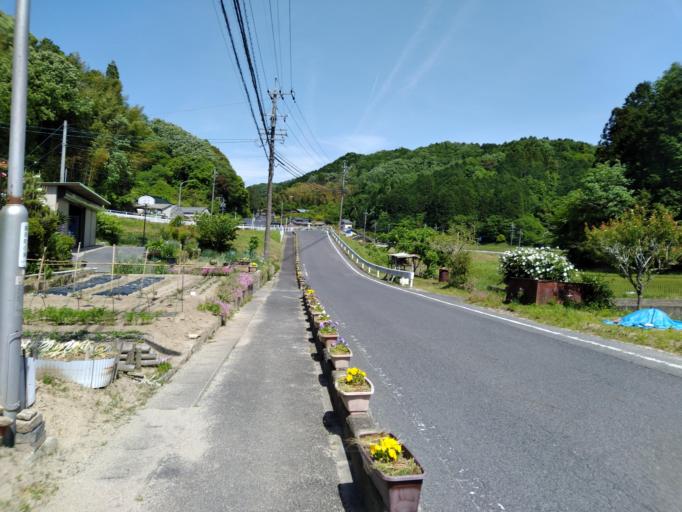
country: JP
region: Gifu
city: Toki
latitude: 35.2431
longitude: 137.2198
